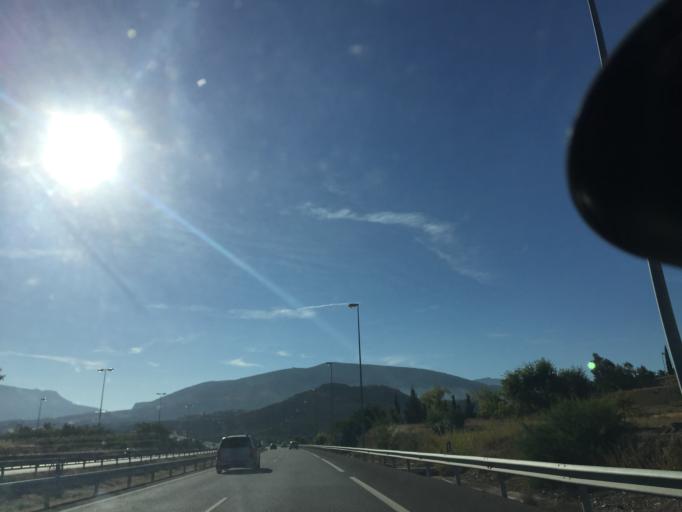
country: ES
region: Andalusia
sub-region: Provincia de Jaen
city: Jaen
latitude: 37.7821
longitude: -3.7536
